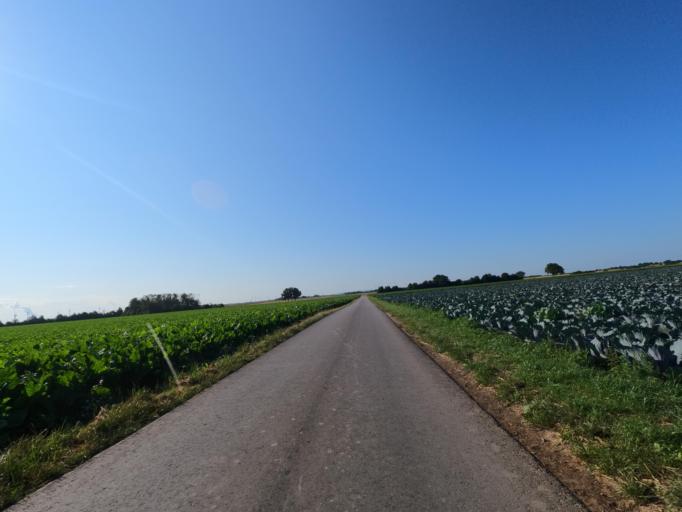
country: DE
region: North Rhine-Westphalia
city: Erkelenz
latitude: 51.0770
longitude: 6.3663
